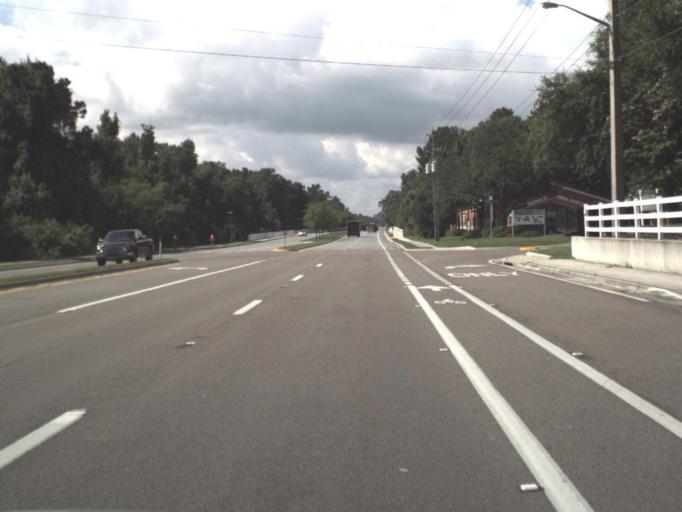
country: US
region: Florida
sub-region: Saint Johns County
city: Fruit Cove
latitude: 30.1052
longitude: -81.6269
